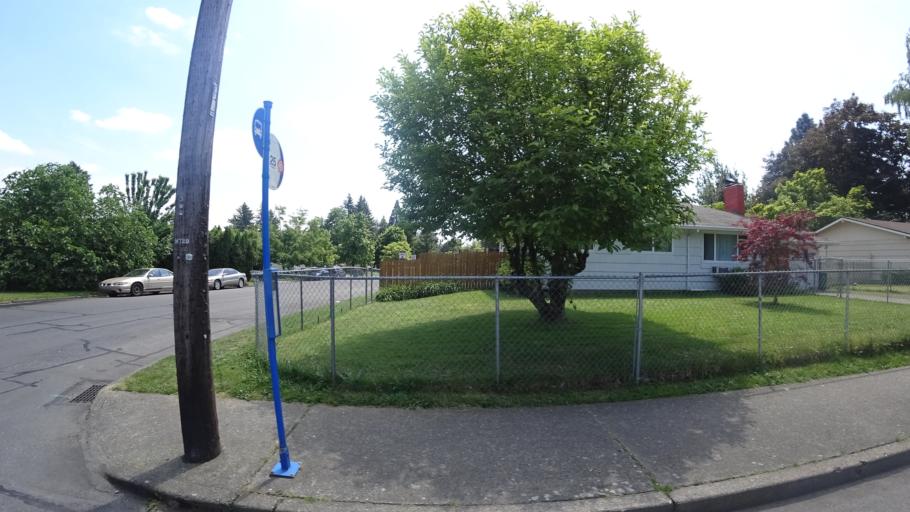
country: US
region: Oregon
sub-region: Multnomah County
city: Fairview
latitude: 45.5264
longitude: -122.4907
